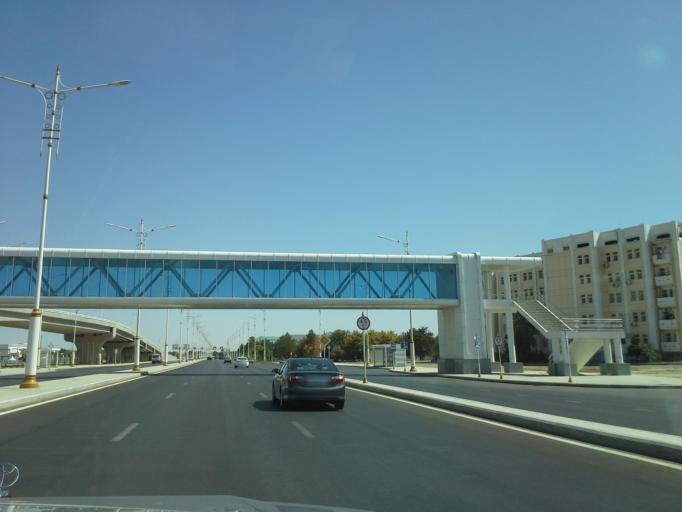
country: TM
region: Ahal
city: Ashgabat
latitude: 37.9257
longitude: 58.4319
